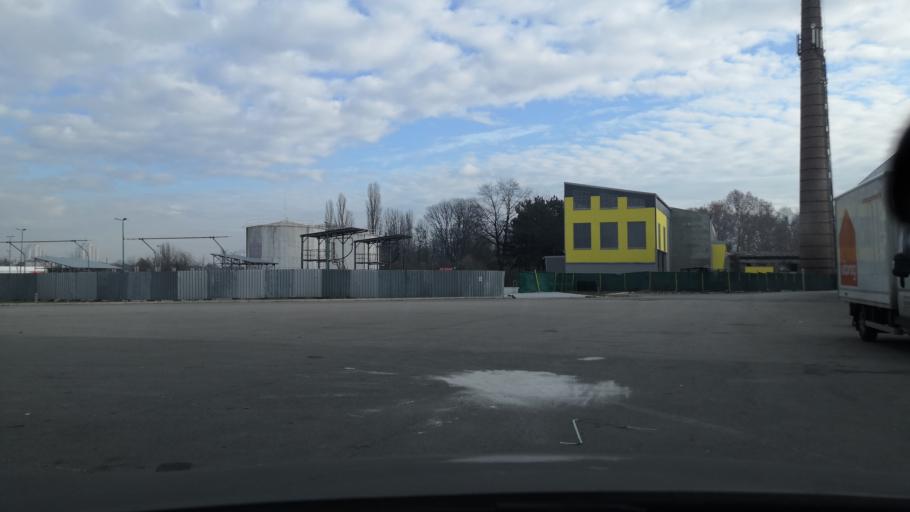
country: RS
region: Central Serbia
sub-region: Belgrade
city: Zemun
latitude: 44.8350
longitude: 20.3687
